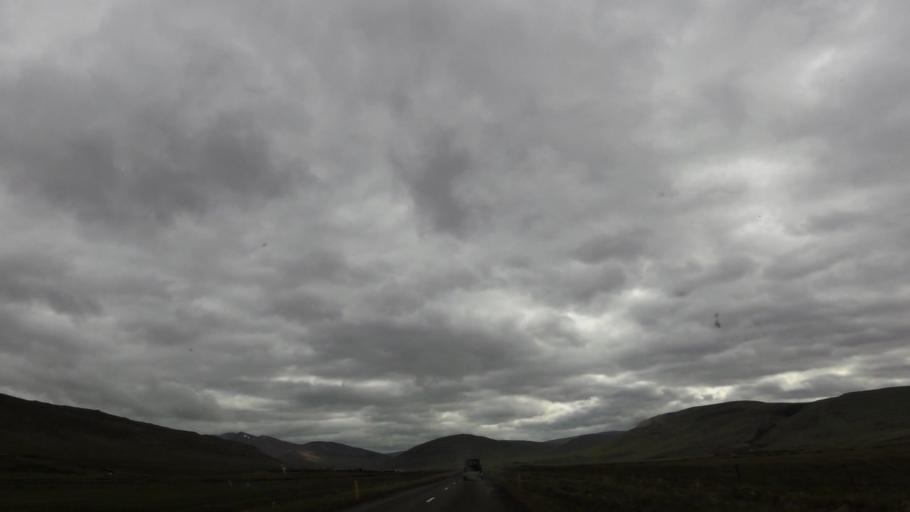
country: IS
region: West
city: Borgarnes
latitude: 65.0080
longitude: -21.6364
